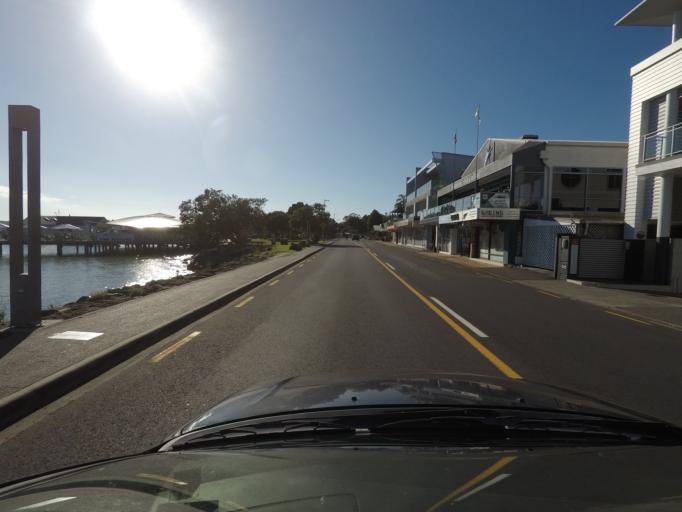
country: NZ
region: Northland
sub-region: Far North District
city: Paihia
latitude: -35.2807
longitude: 174.0911
